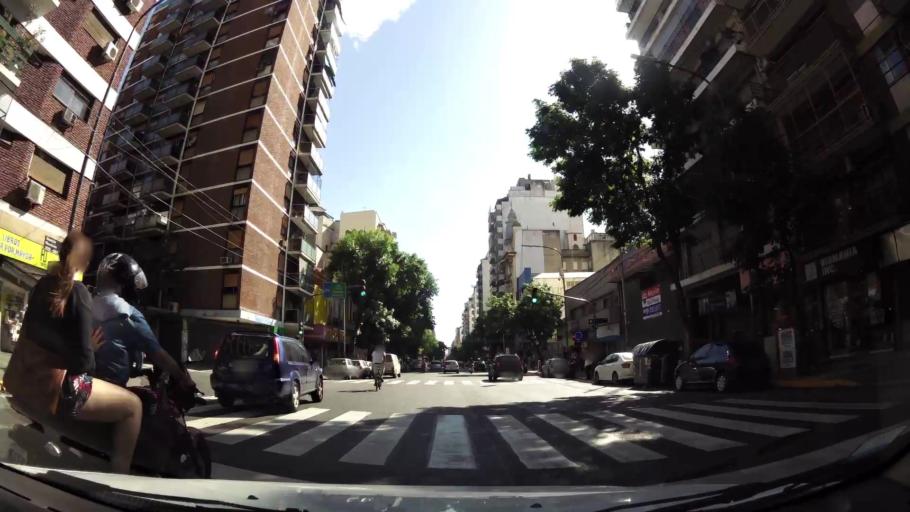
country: AR
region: Buenos Aires F.D.
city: Buenos Aires
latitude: -34.6121
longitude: -58.4223
